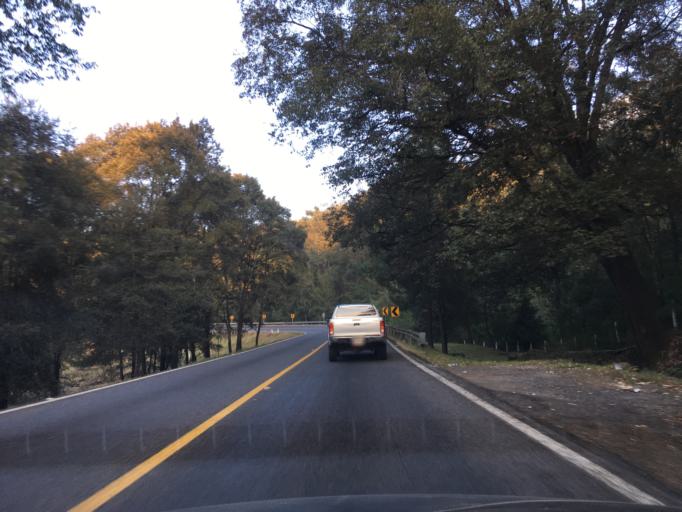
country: MX
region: Michoacan
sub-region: Patzcuaro
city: Santa Maria Huiramangaro (San Juan Tumbio)
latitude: 19.4933
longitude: -101.7154
